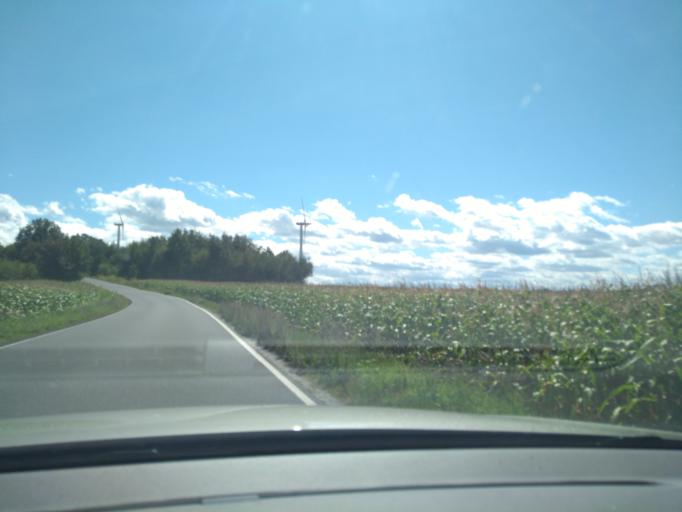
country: DE
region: Saxony
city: Lichtenberg
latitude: 51.1393
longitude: 13.9563
